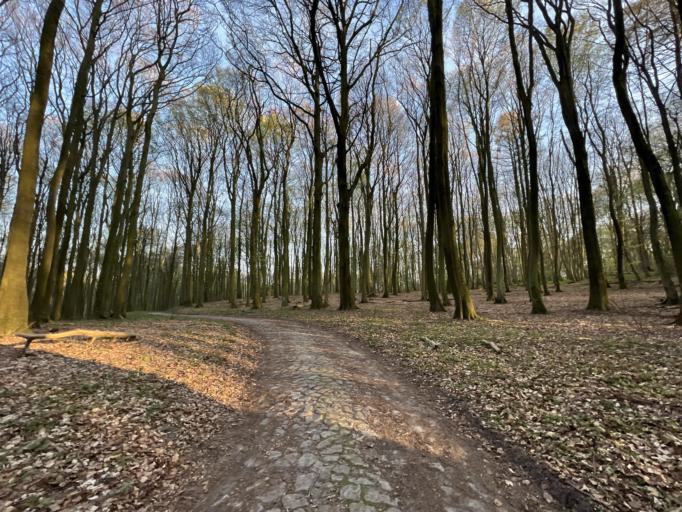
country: DE
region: Mecklenburg-Vorpommern
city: Sassnitz
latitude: 54.5315
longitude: 13.6529
